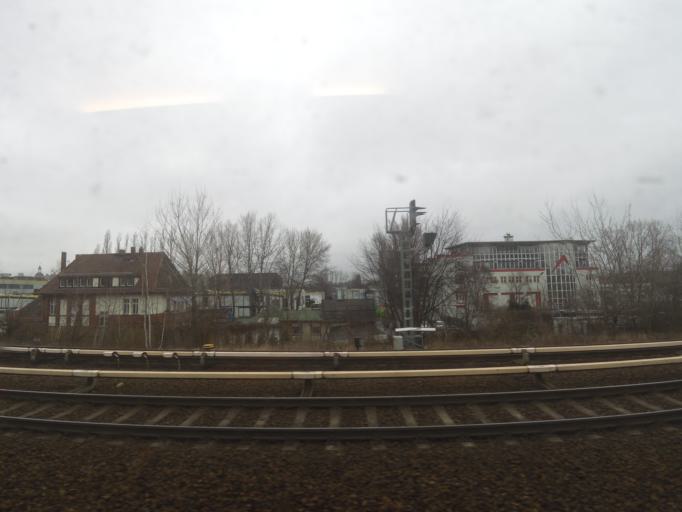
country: DE
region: Berlin
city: Spandau
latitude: 52.5316
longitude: 13.2126
